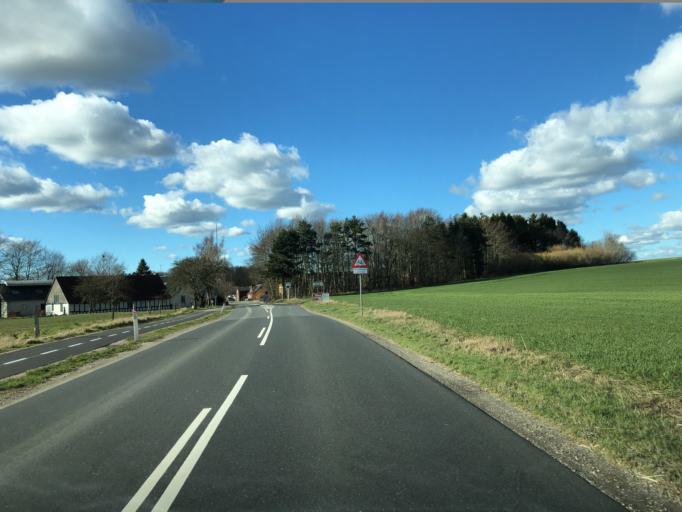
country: DK
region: Central Jutland
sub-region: Favrskov Kommune
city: Hadsten
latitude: 56.2897
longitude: 10.0072
